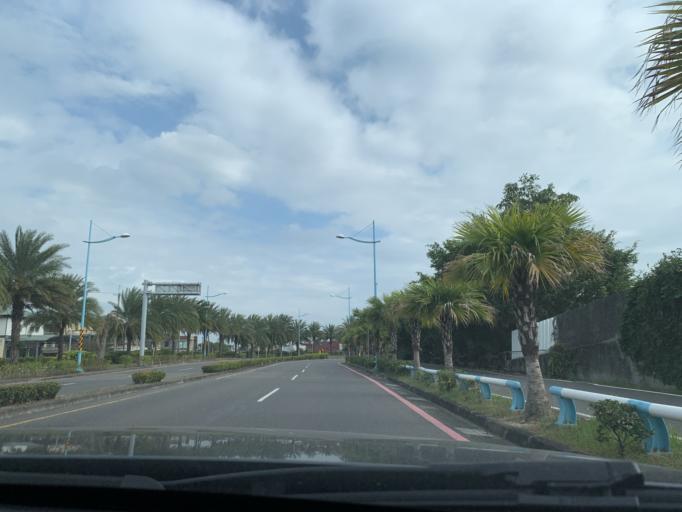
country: TW
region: Taiwan
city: Fengshan
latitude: 22.4556
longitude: 120.4848
